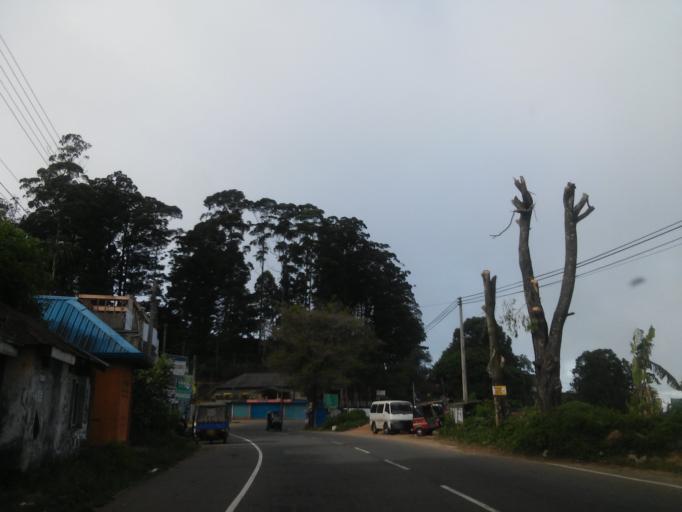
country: LK
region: Uva
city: Haputale
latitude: 6.7716
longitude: 80.9619
